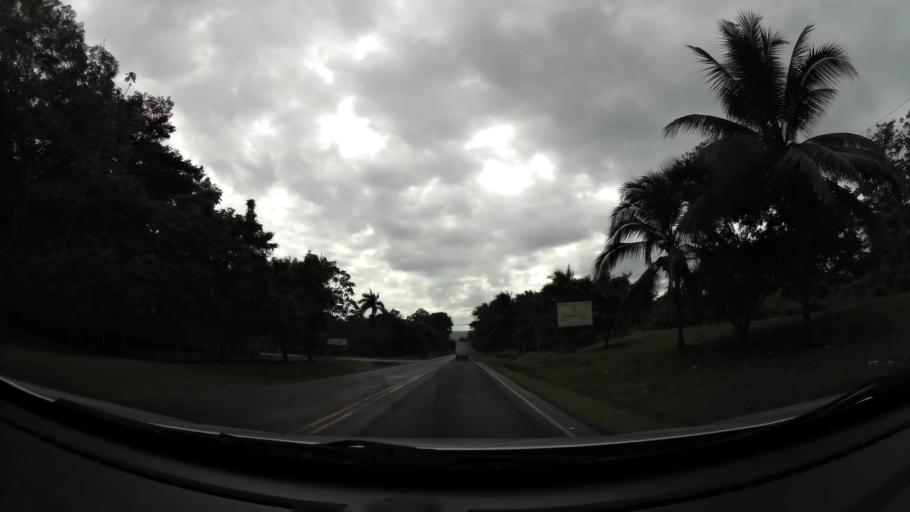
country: CR
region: Limon
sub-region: Canton de Siquirres
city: Siquirres
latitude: 10.1188
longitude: -83.5488
